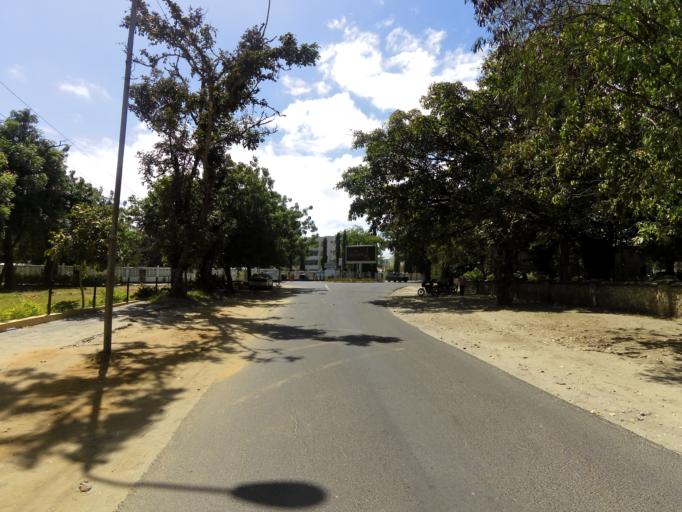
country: TZ
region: Dar es Salaam
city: Dar es Salaam
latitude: -6.8111
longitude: 39.2952
